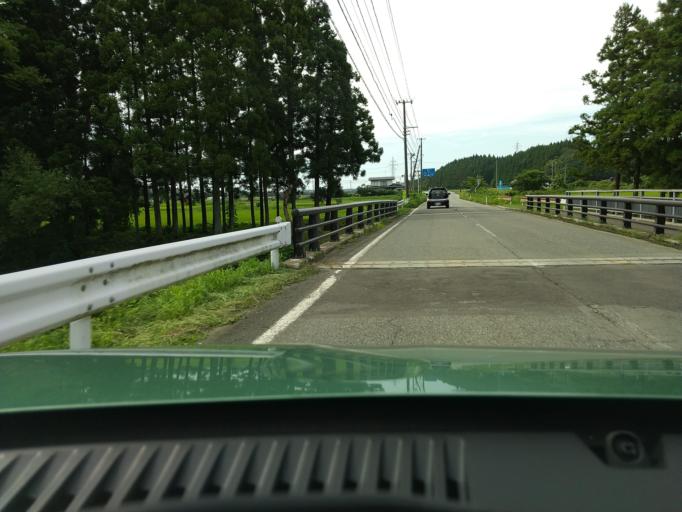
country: JP
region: Akita
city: Akita Shi
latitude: 39.7900
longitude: 140.1132
